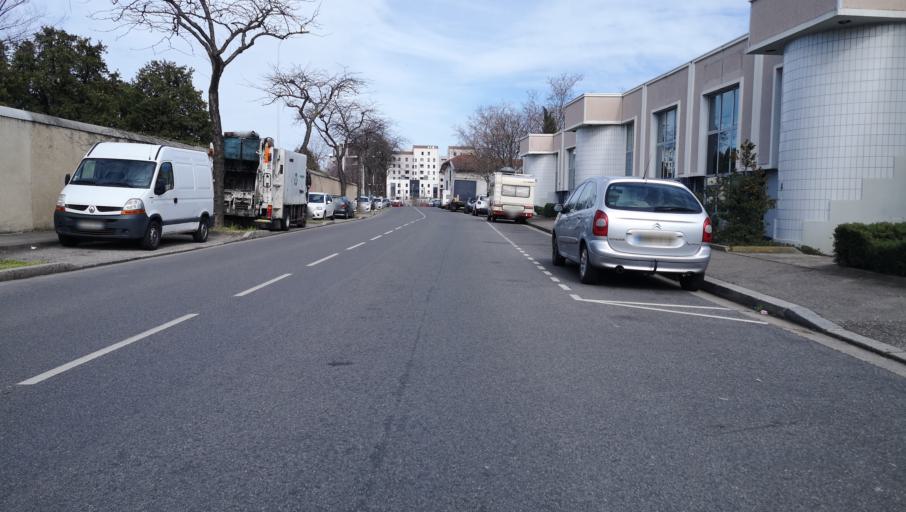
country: FR
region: Rhone-Alpes
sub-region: Departement du Rhone
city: Lyon
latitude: 45.7372
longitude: 4.8583
